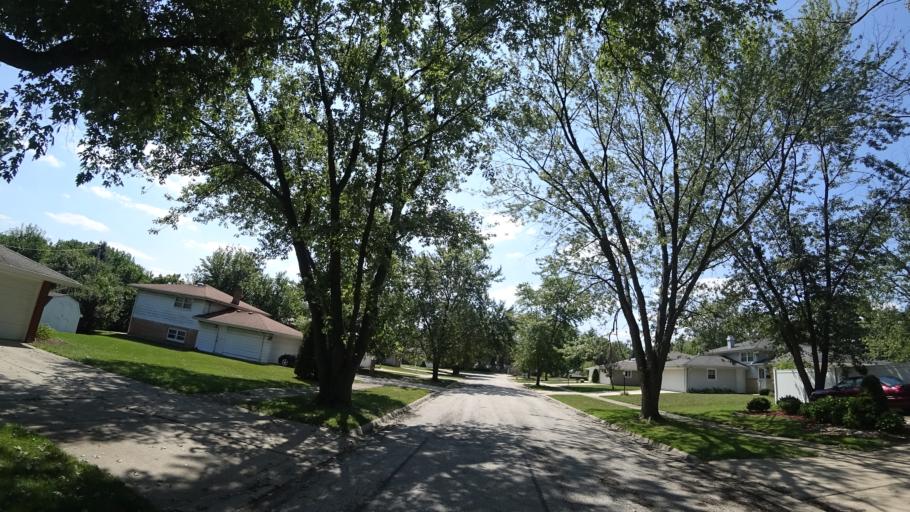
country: US
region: Illinois
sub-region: Cook County
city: Orland Park
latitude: 41.6285
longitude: -87.8423
